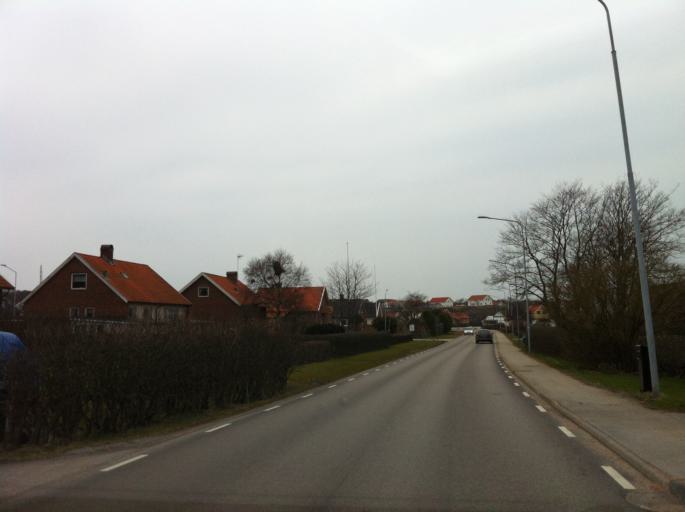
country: SE
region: Vaestra Goetaland
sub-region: Orust
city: Henan
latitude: 58.1767
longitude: 11.6971
